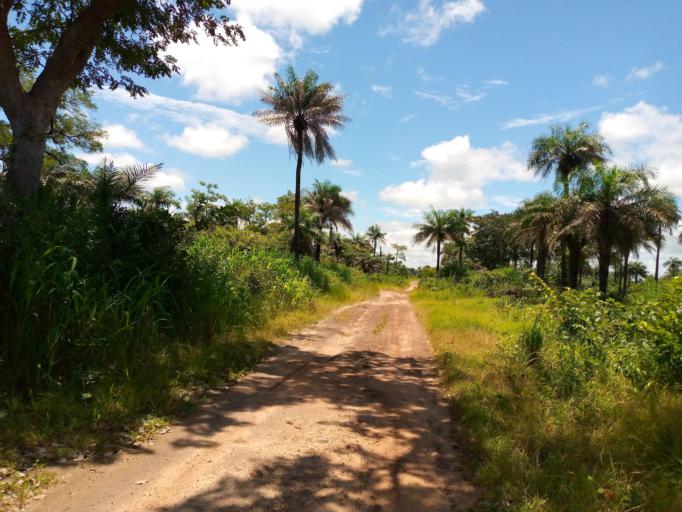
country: SL
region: Northern Province
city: Binkolo
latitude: 9.0670
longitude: -12.1486
